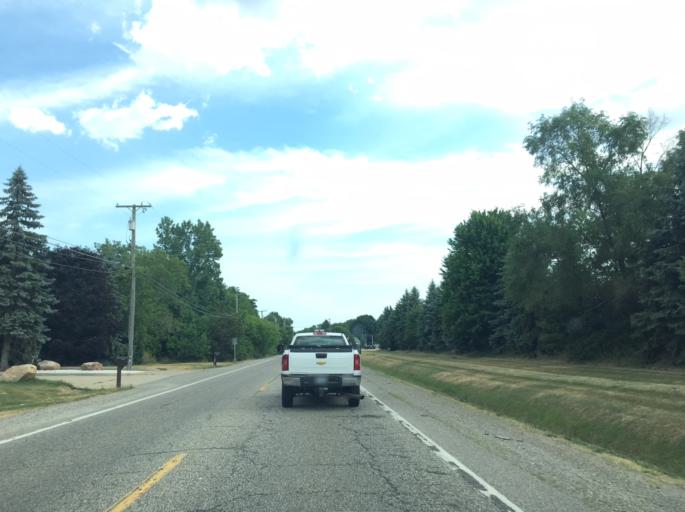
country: US
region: Michigan
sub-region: Macomb County
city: Sterling Heights
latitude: 42.5976
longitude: -83.0184
